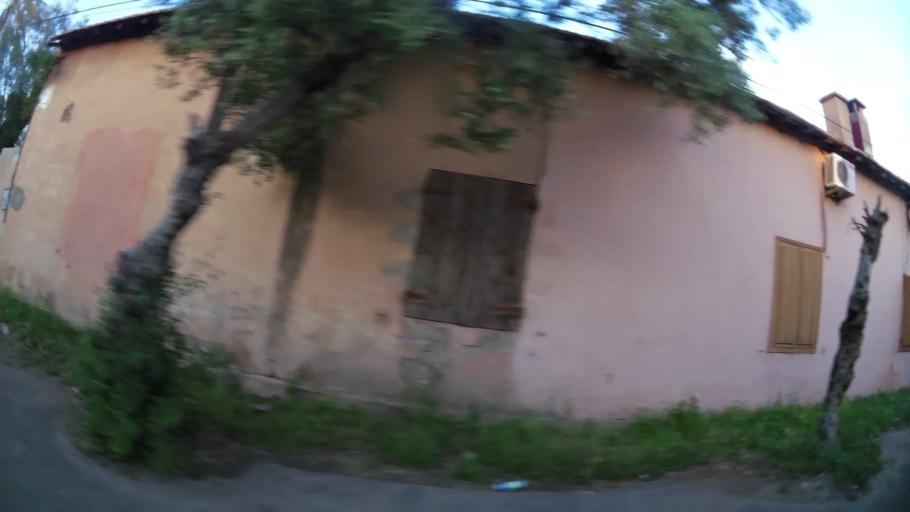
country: MA
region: Marrakech-Tensift-Al Haouz
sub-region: Marrakech
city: Marrakesh
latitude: 31.6367
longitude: -8.0235
